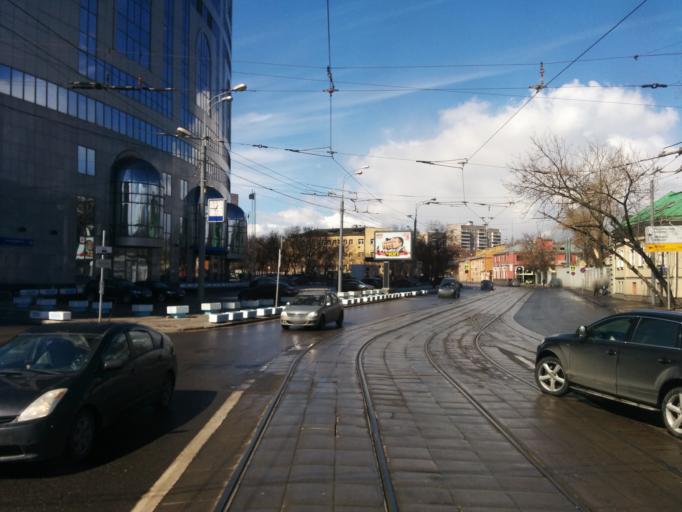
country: RU
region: Moscow
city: Sokol'niki
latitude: 55.7765
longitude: 37.6492
